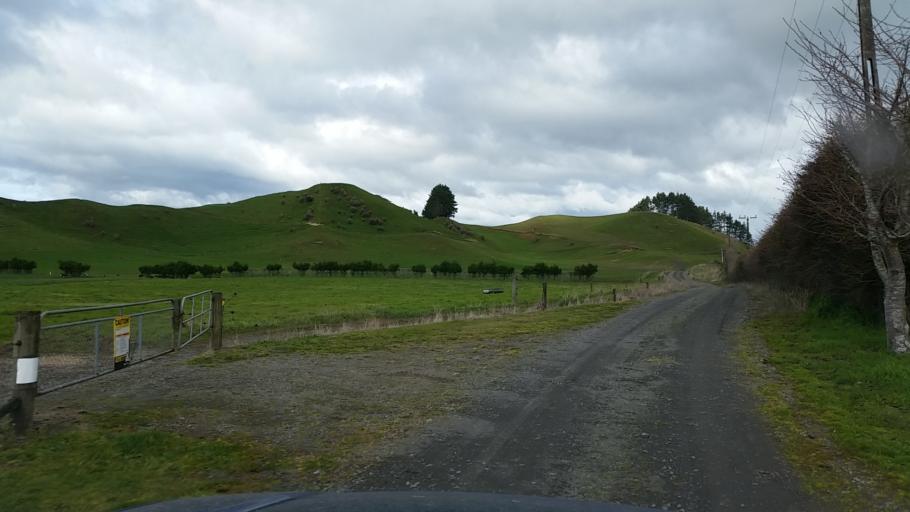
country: NZ
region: Taranaki
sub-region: South Taranaki District
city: Eltham
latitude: -39.3505
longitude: 174.3839
